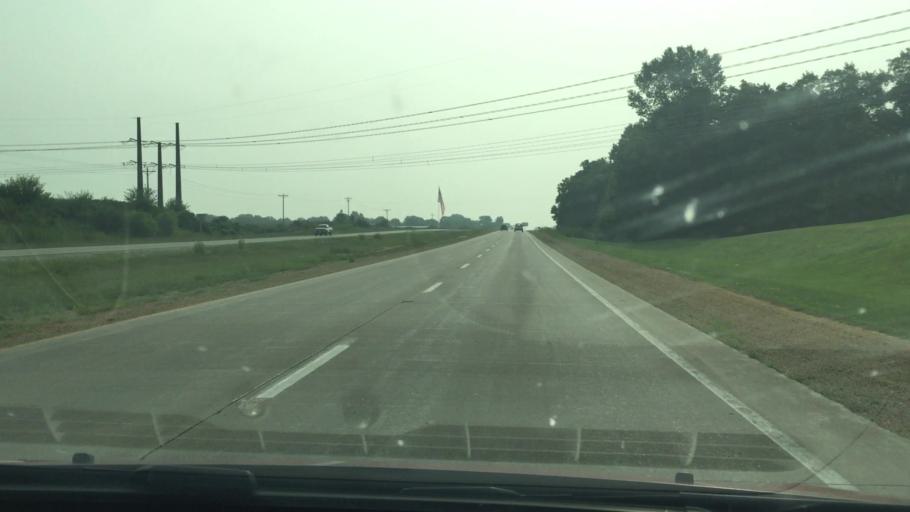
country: US
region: Iowa
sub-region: Scott County
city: Buffalo
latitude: 41.5089
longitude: -90.7002
